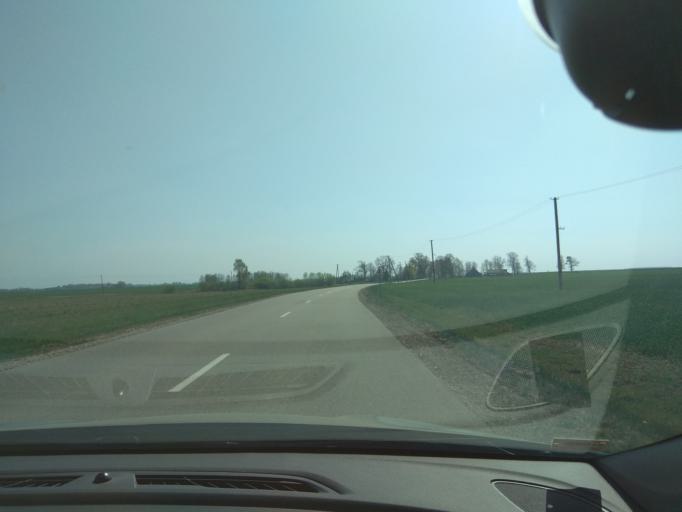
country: LT
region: Panevezys
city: Pasvalys
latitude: 55.9687
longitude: 24.2083
